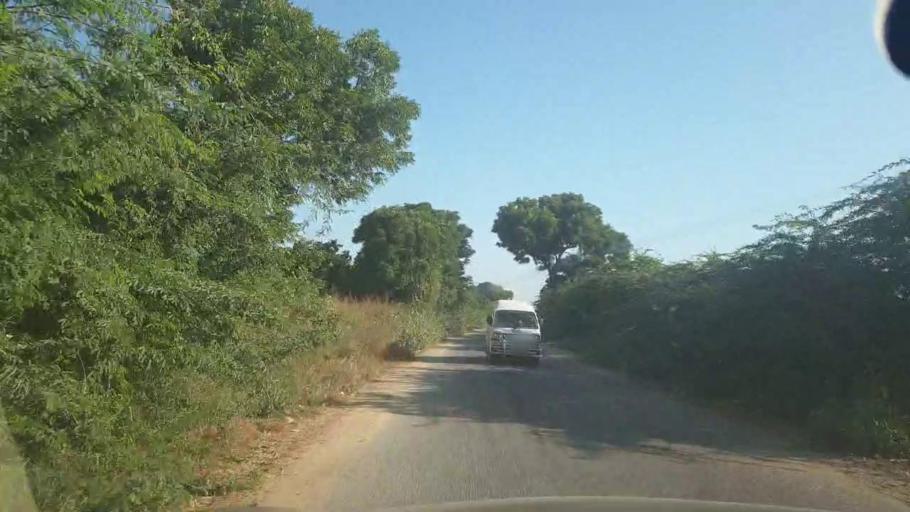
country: PK
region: Sindh
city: Malir Cantonment
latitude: 25.1045
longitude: 67.2590
